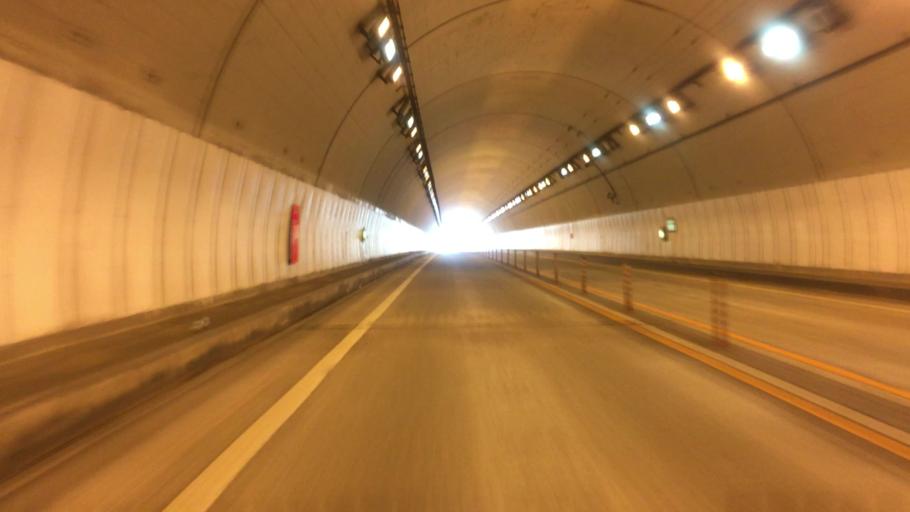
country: JP
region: Kyoto
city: Fukuchiyama
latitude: 35.2282
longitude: 135.0271
